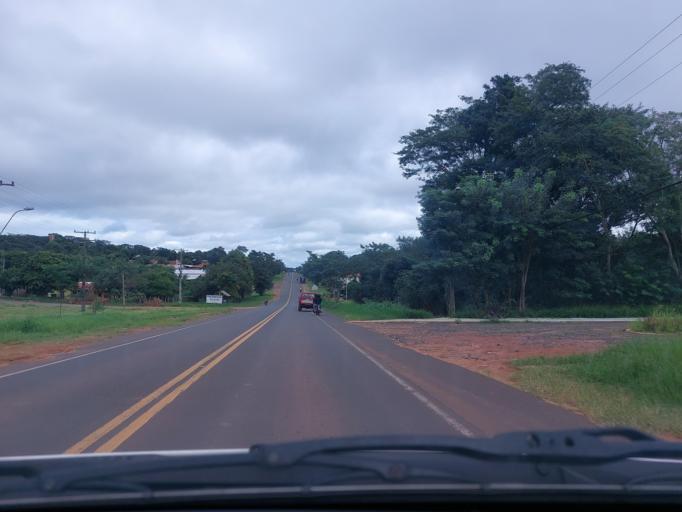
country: PY
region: San Pedro
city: Guayaybi
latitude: -24.6631
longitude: -56.4216
